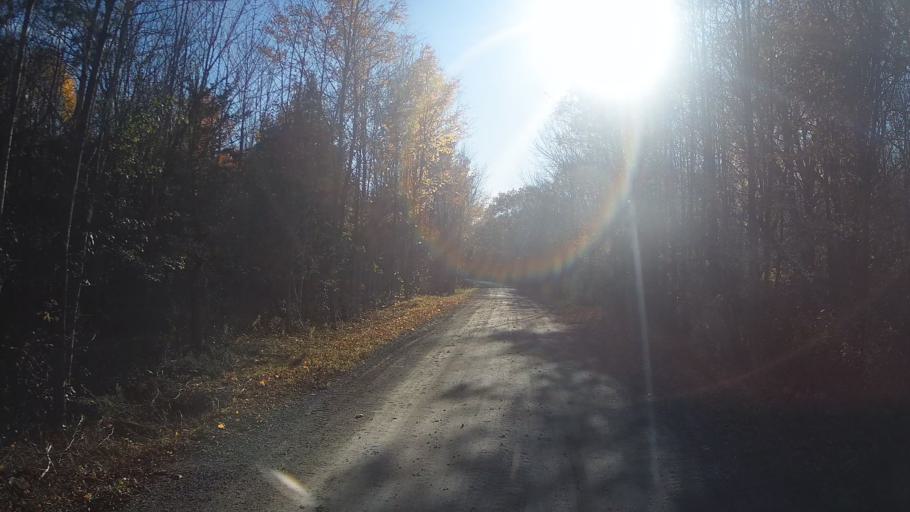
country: CA
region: Ontario
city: Perth
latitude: 44.7184
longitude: -76.4133
